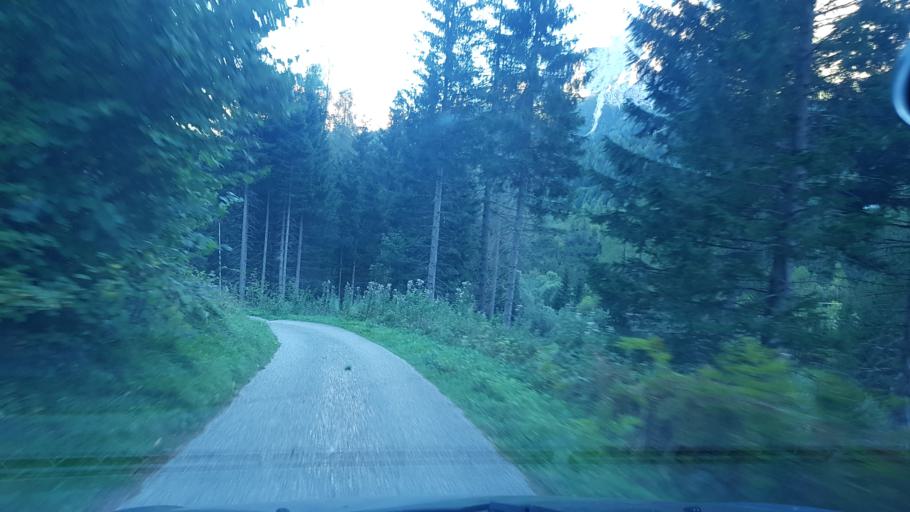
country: IT
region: Veneto
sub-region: Provincia di Belluno
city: Fusine
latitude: 46.3465
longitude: 12.0935
